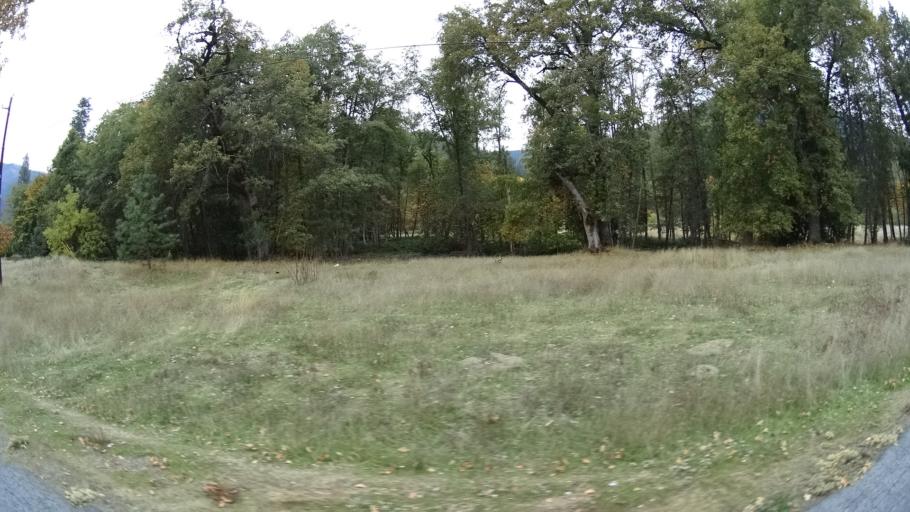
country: US
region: California
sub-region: Siskiyou County
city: Happy Camp
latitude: 41.8393
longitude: -123.2095
